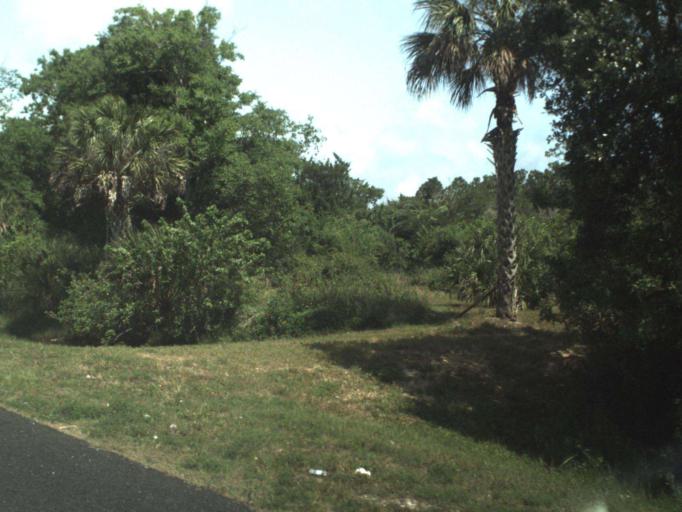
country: US
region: Florida
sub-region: Volusia County
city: Ormond Beach
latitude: 29.2937
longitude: -81.0750
